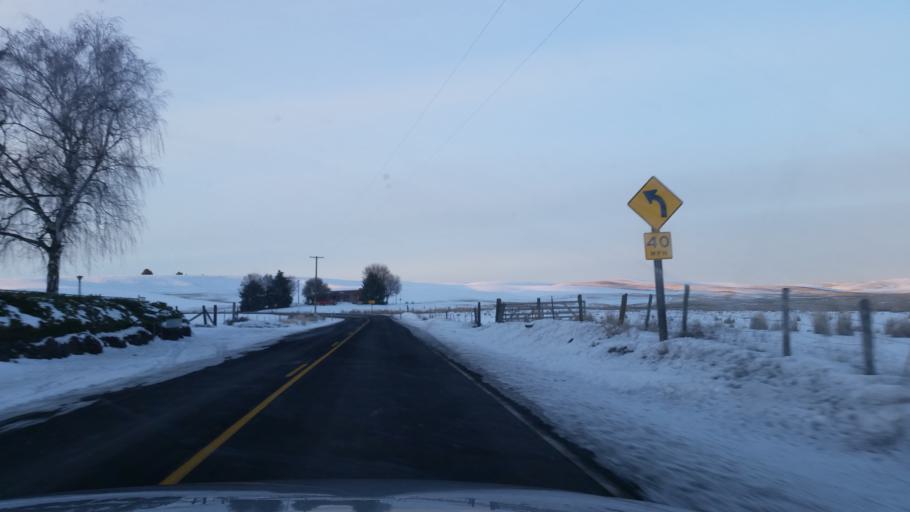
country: US
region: Washington
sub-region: Spokane County
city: Cheney
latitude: 47.1390
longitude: -117.8291
